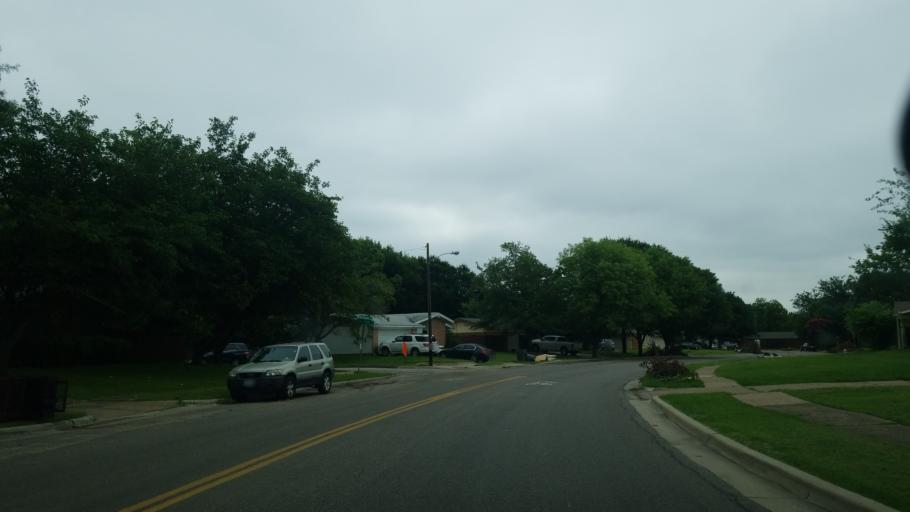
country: US
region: Texas
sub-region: Dallas County
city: Farmers Branch
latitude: 32.9036
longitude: -96.8712
